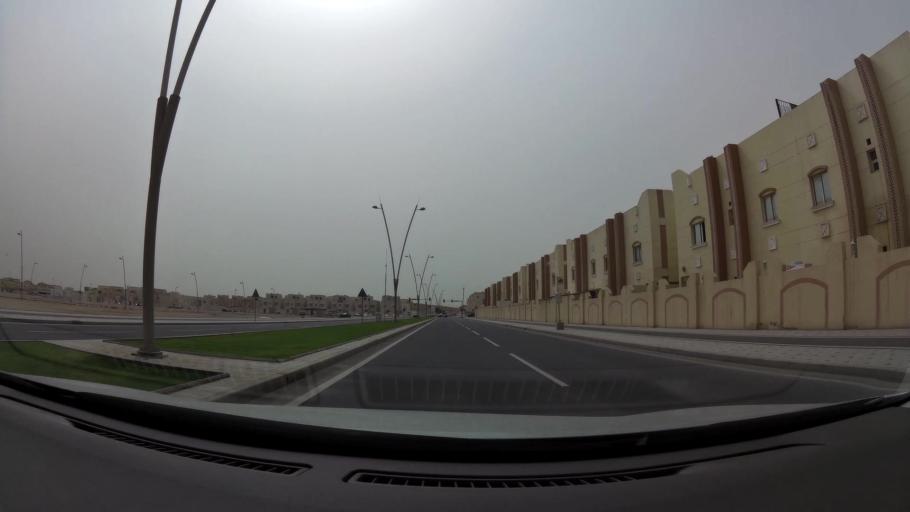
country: QA
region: Baladiyat ad Dawhah
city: Doha
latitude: 25.2314
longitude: 51.5438
